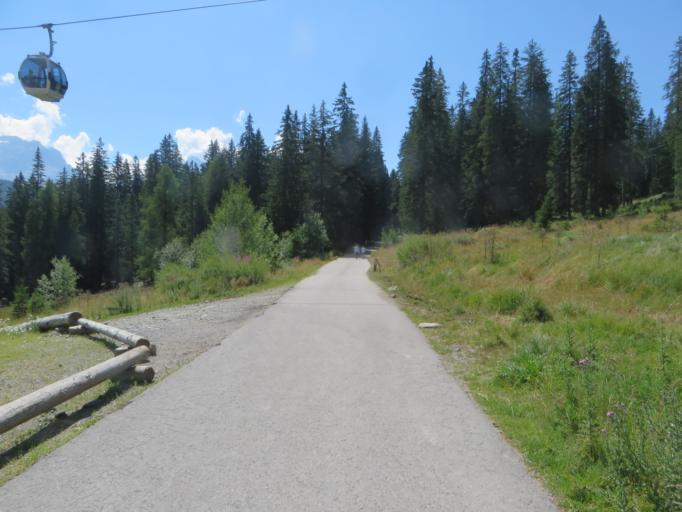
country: IT
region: Trentino-Alto Adige
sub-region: Provincia di Trento
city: Carisolo
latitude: 46.2304
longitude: 10.8161
